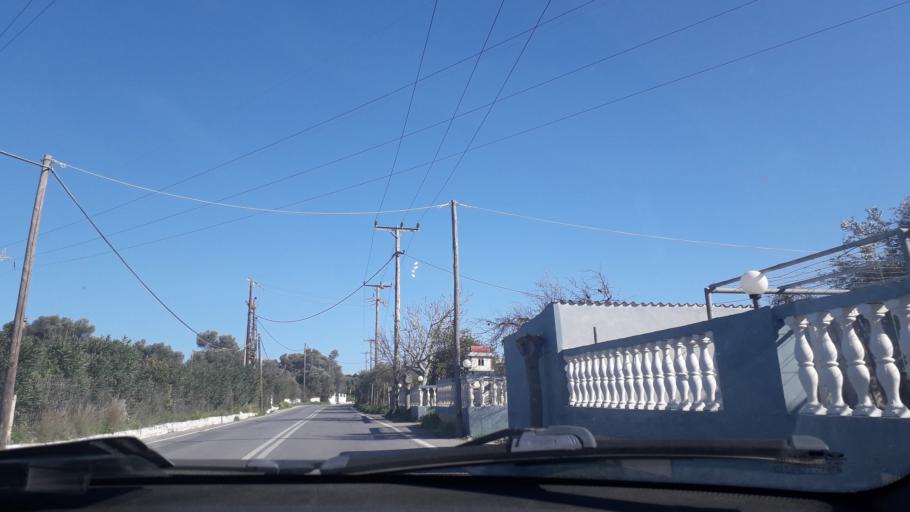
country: GR
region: Crete
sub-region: Nomos Rethymnis
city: Rethymno
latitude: 35.3603
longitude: 24.5478
